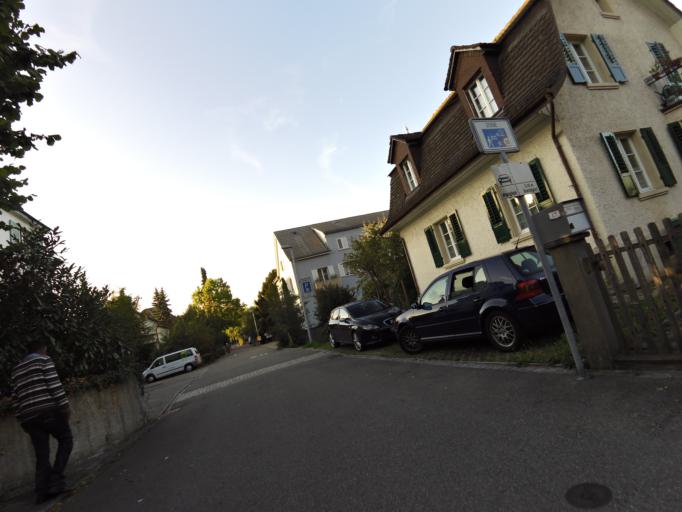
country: CH
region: Aargau
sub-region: Bezirk Aarau
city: Aarau
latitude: 47.3956
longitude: 8.0521
